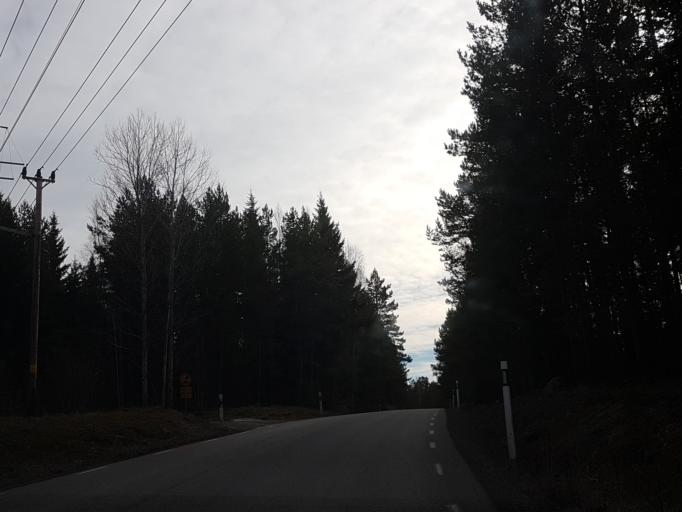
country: SE
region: Stockholm
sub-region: Norrtalje Kommun
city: Norrtalje
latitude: 59.6812
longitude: 18.8362
